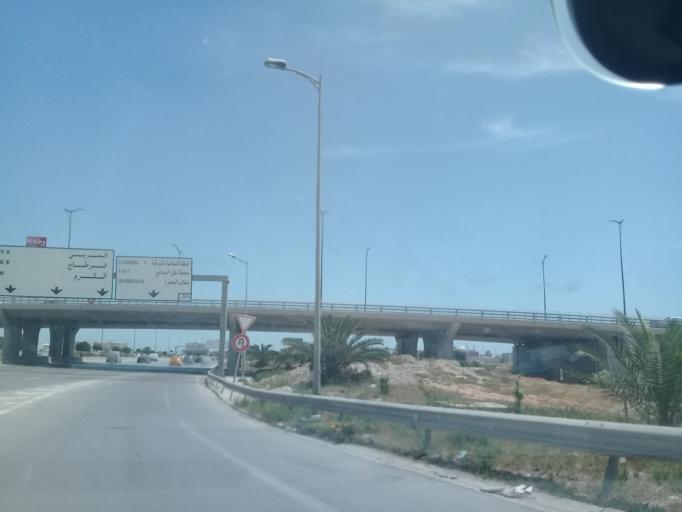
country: TN
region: Ariana
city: Ariana
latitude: 36.8318
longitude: 10.2149
